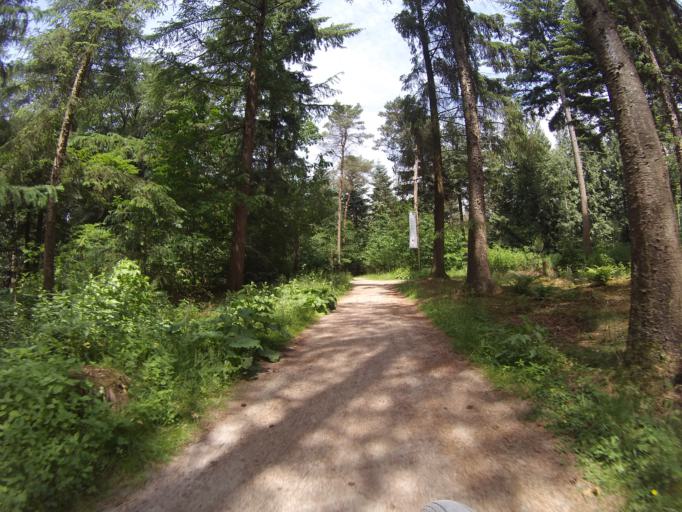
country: NL
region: Gelderland
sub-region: Gemeente Ede
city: Lunteren
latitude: 52.0852
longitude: 5.6494
